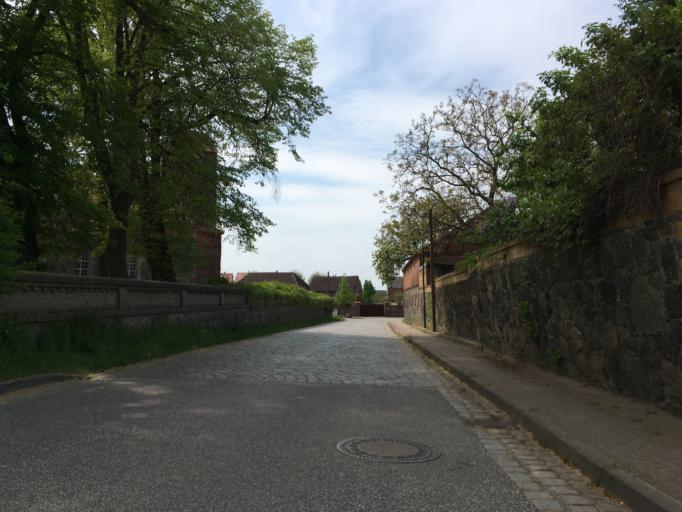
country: DE
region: Brandenburg
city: Biesenthal
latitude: 52.7346
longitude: 13.6686
